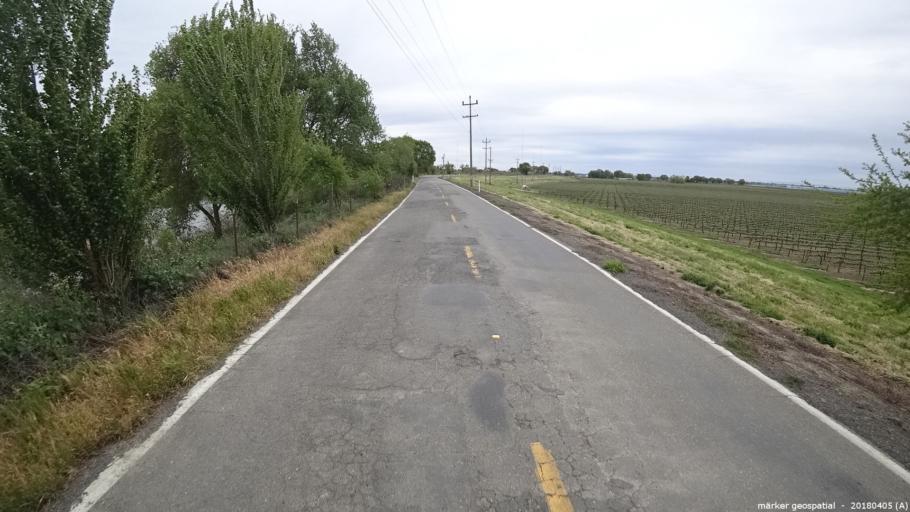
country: US
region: California
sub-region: Sacramento County
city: Walnut Grove
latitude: 38.3184
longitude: -121.5192
